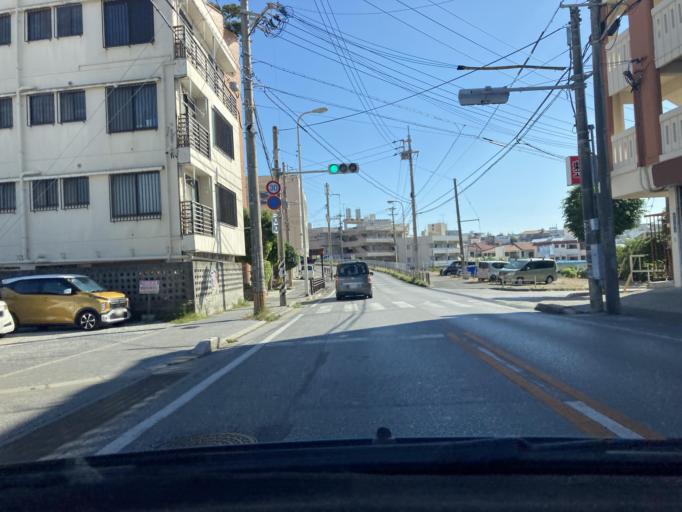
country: JP
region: Okinawa
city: Tomigusuku
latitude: 26.1847
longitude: 127.6608
